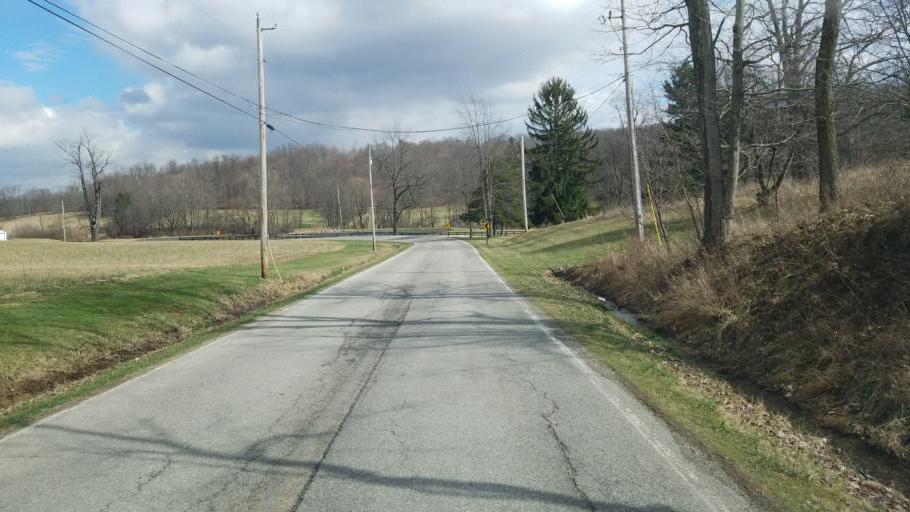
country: US
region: Ohio
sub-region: Richland County
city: Lincoln Heights
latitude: 40.6968
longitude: -82.4337
